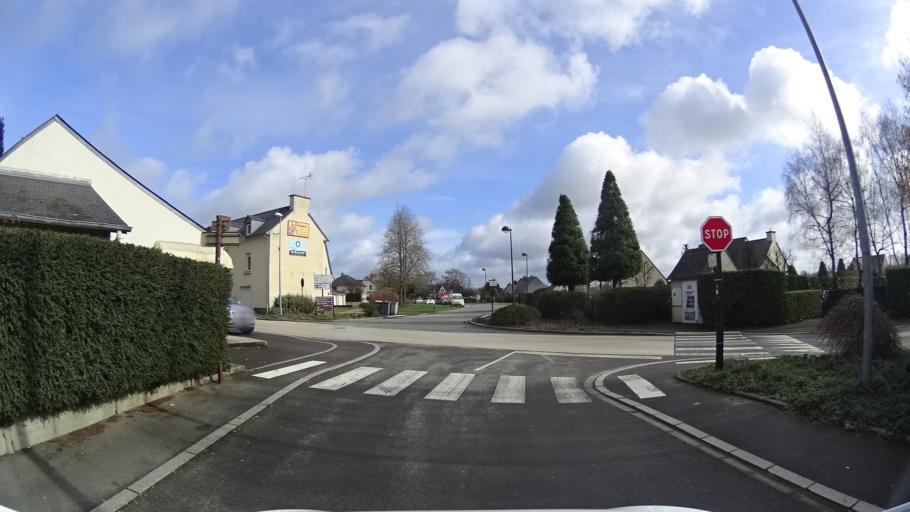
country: FR
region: Brittany
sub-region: Departement d'Ille-et-Vilaine
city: Romille
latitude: 48.2125
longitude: -1.8914
